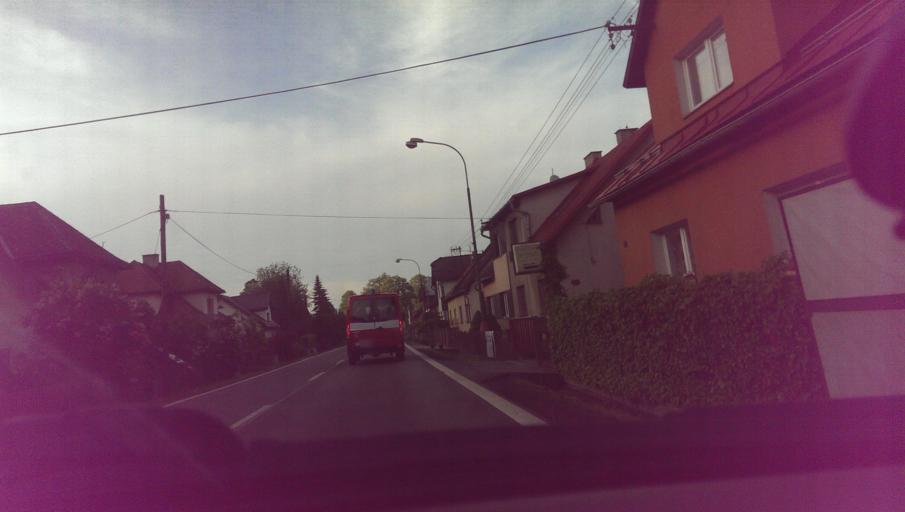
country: CZ
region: Zlin
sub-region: Okres Vsetin
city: Vsetin
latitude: 49.3043
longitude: 18.0025
